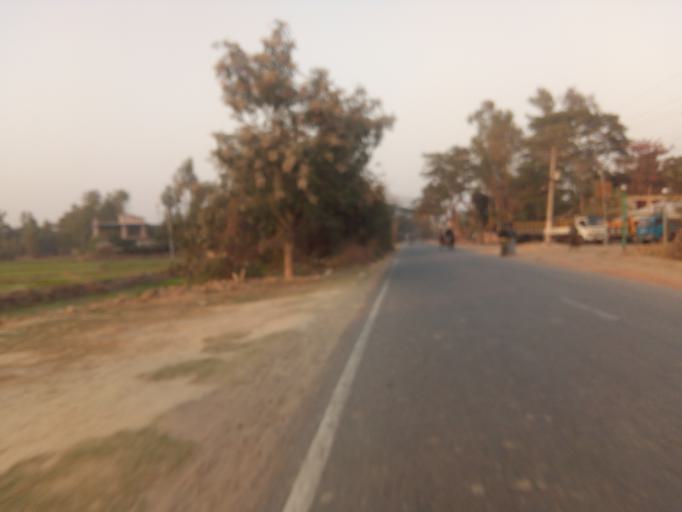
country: BD
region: Rajshahi
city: Bogra
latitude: 24.6413
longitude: 89.2522
